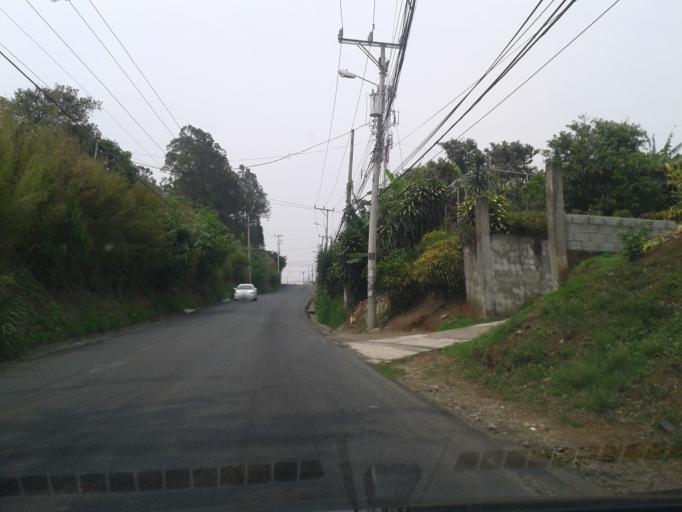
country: CR
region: Heredia
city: San Francisco
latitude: 9.9820
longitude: -84.1339
